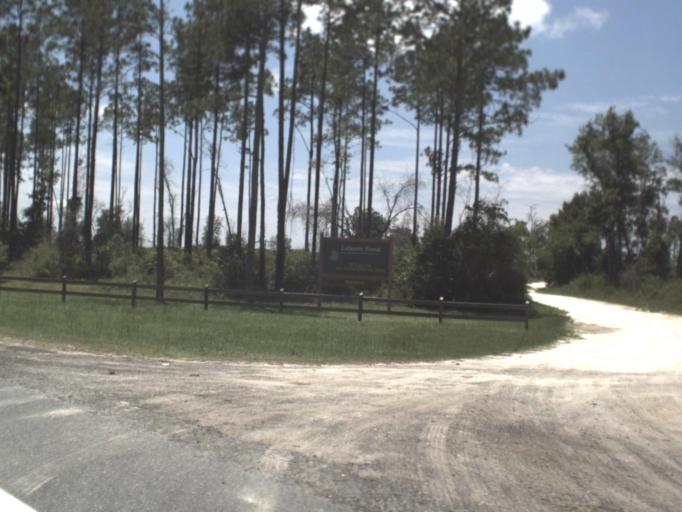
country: US
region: Florida
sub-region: Dixie County
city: Cross City
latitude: 29.8391
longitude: -82.9683
